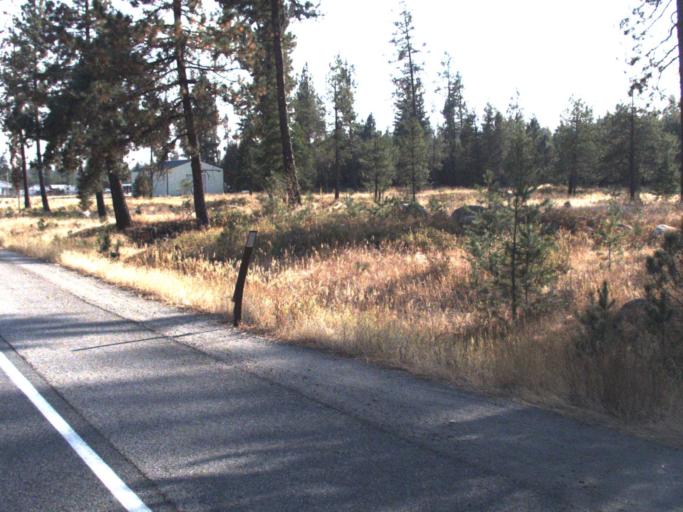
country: US
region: Washington
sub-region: Spokane County
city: Deer Park
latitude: 47.9839
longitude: -117.3496
